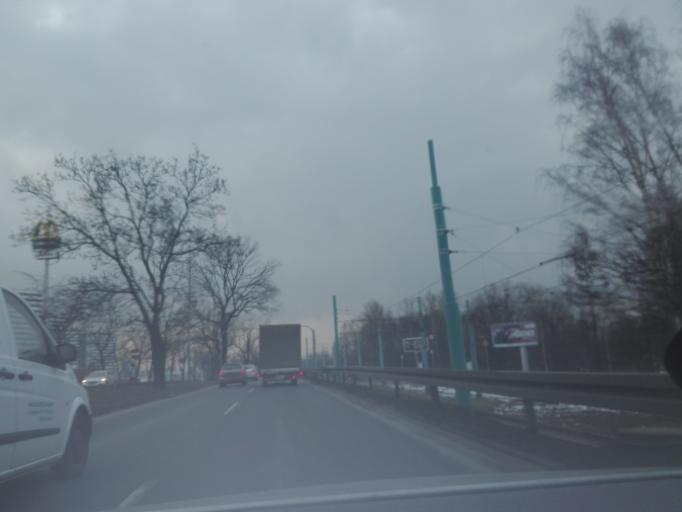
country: PL
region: Silesian Voivodeship
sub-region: Chorzow
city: Chorzow
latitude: 50.2838
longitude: 18.9736
